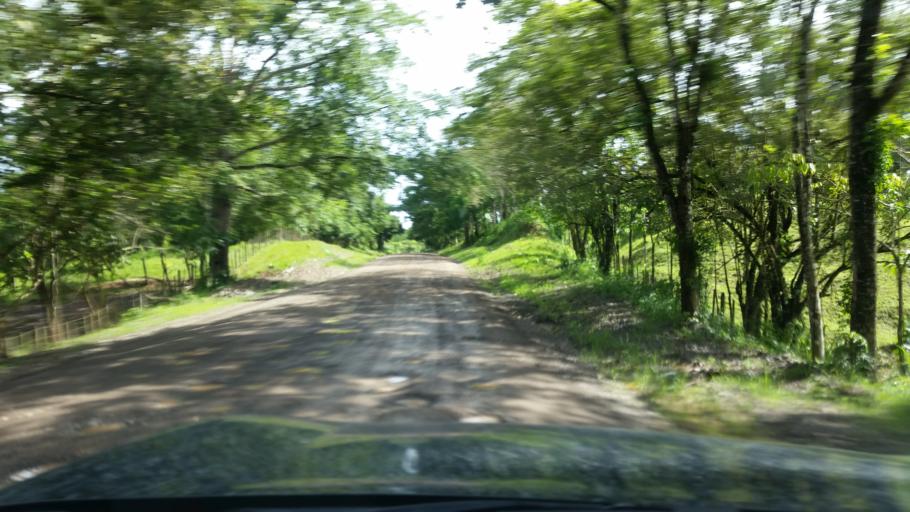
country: NI
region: Atlantico Norte (RAAN)
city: Siuna
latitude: 13.6938
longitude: -84.7857
